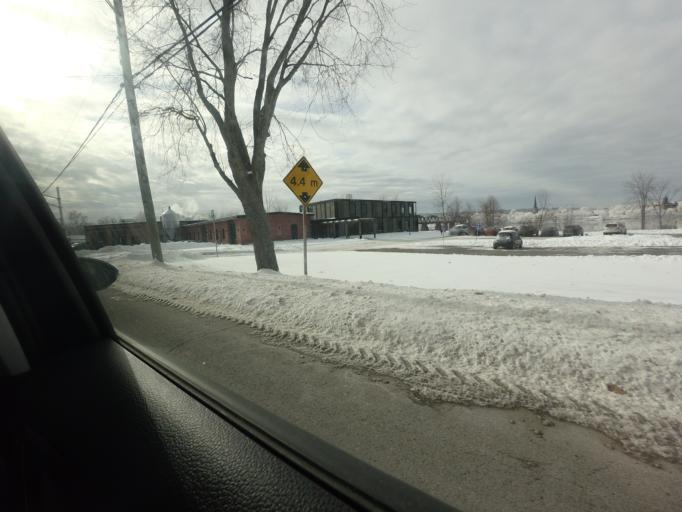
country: CA
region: New Brunswick
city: Fredericton
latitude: 45.9594
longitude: -66.6243
